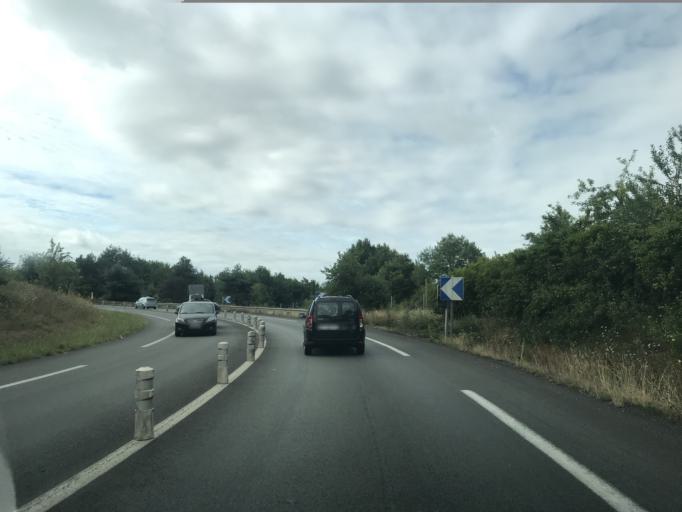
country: FR
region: Poitou-Charentes
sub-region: Departement de la Vienne
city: Vouneuil-sous-Biard
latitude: 46.5551
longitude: 0.2809
